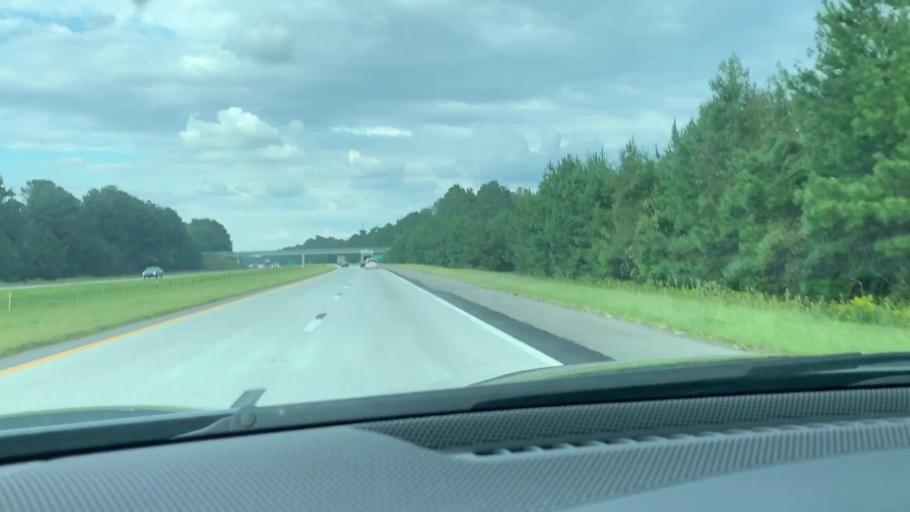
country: US
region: South Carolina
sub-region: Dorchester County
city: Saint George
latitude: 33.2924
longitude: -80.5587
